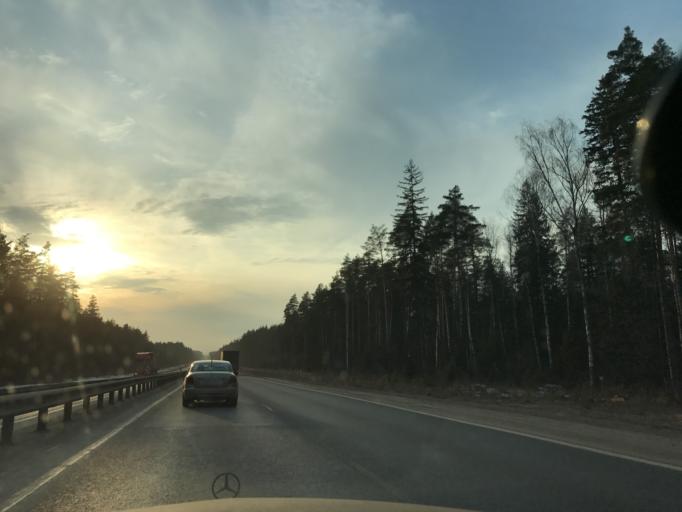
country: RU
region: Vladimir
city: Petushki
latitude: 55.9299
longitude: 39.3479
